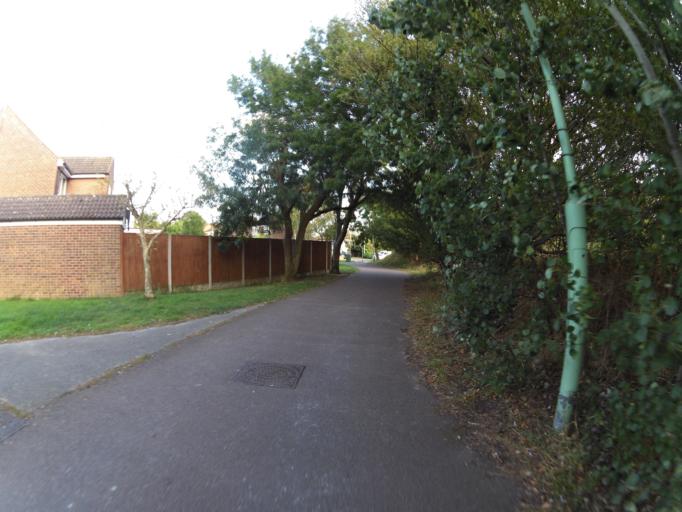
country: GB
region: England
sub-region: Suffolk
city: Kessingland
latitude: 52.4539
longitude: 1.7086
